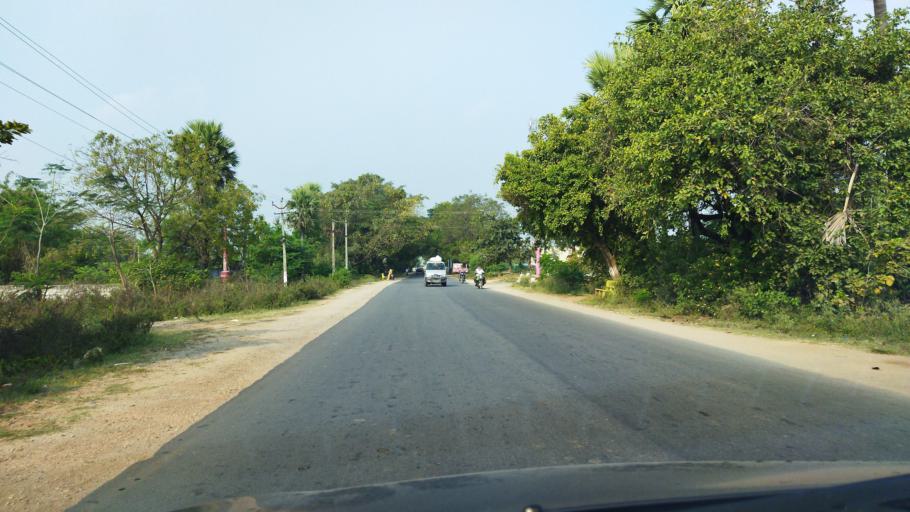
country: IN
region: Telangana
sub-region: Nalgonda
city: Nalgonda
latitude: 17.1674
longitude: 79.4095
